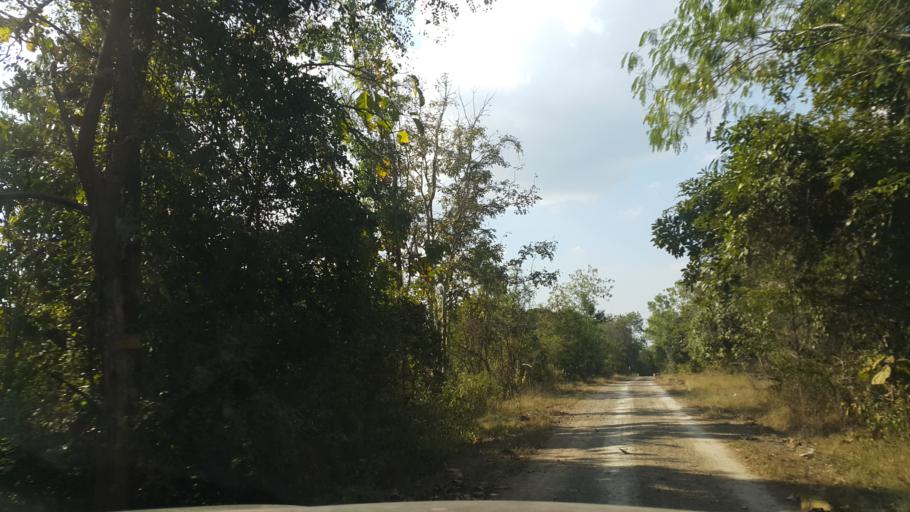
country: TH
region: Lamphun
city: Ban Thi
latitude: 18.5640
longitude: 99.1169
